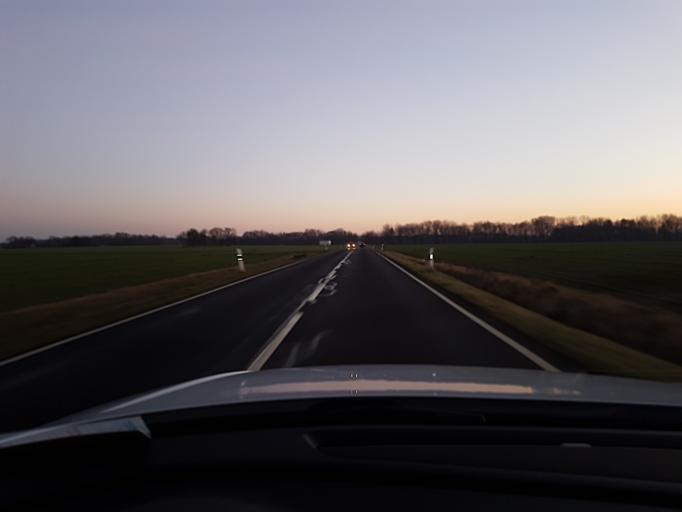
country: DE
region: Mecklenburg-Vorpommern
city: Gingst
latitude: 54.4781
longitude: 13.2918
